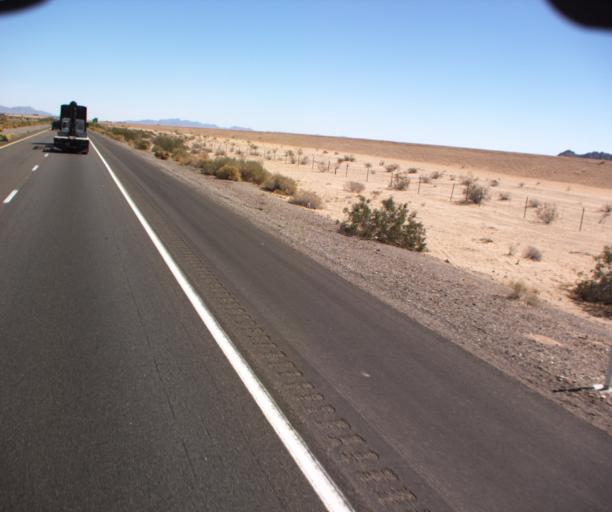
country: US
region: Arizona
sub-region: Yuma County
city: Wellton
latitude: 32.6775
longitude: -114.0405
